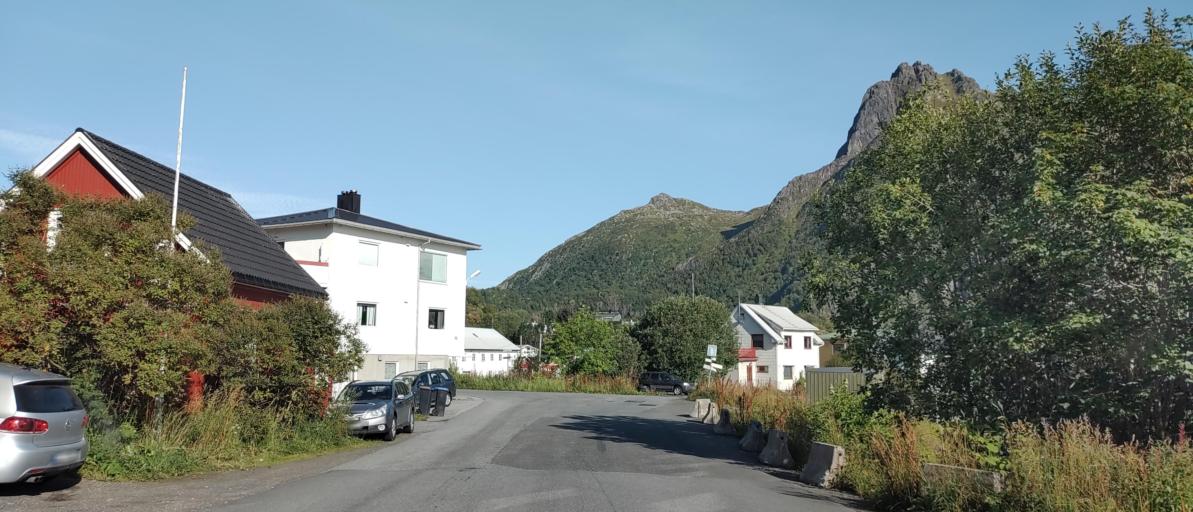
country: NO
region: Nordland
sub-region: Vagan
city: Svolvaer
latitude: 68.2377
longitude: 14.5714
